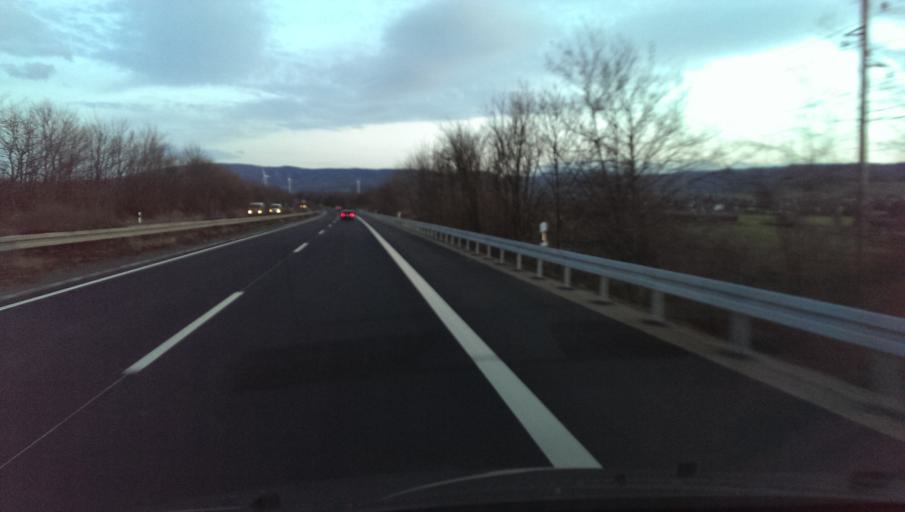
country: DE
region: Lower Saxony
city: Bad Harzburg
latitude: 51.9178
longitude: 10.5213
